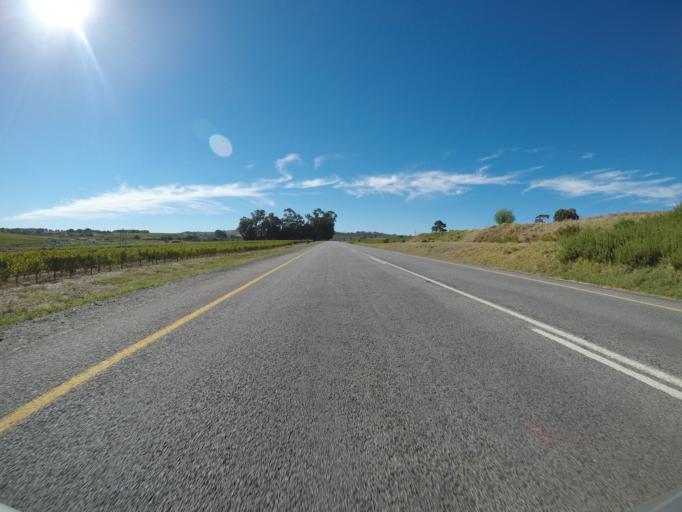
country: ZA
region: Western Cape
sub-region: Cape Winelands District Municipality
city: Stellenbosch
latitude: -33.9861
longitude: 18.7557
